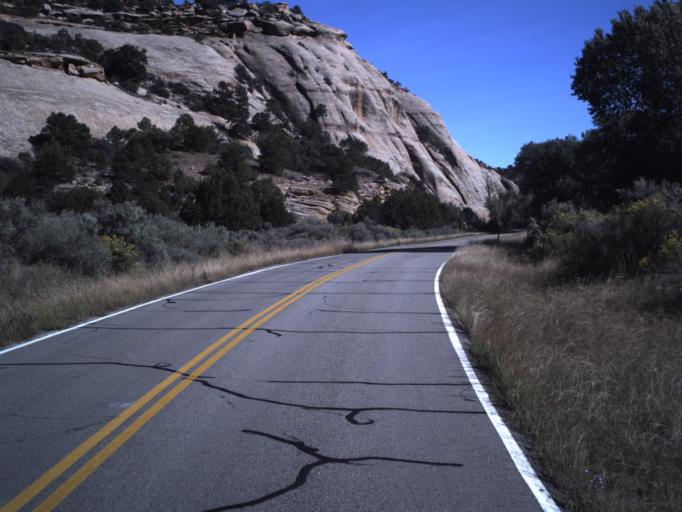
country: US
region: Utah
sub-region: San Juan County
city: Monticello
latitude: 37.9931
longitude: -109.5235
